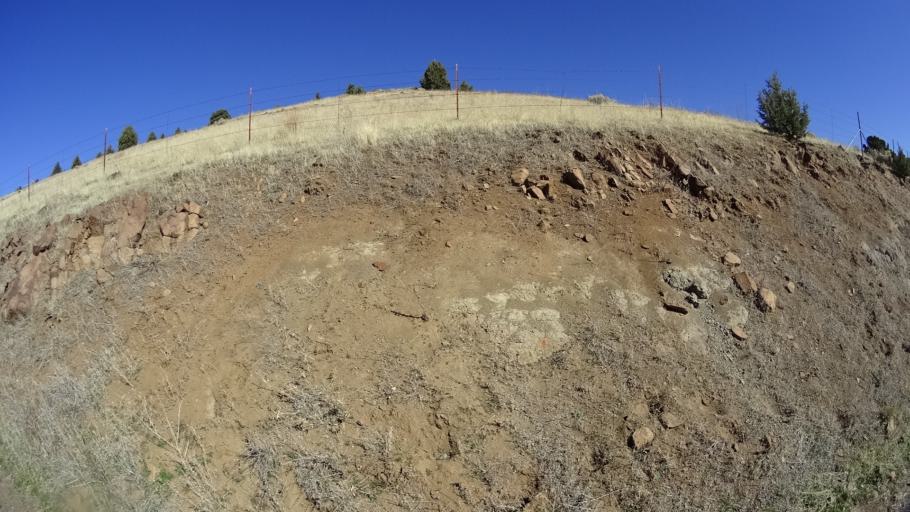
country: US
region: California
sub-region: Siskiyou County
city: Montague
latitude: 41.8244
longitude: -122.3370
